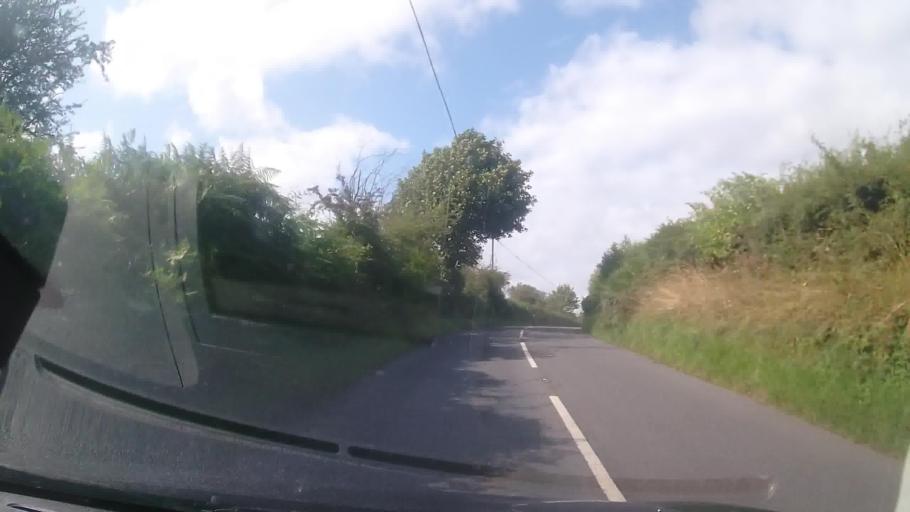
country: GB
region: Wales
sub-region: Sir Powys
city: Knighton
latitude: 52.3707
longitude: -3.0499
